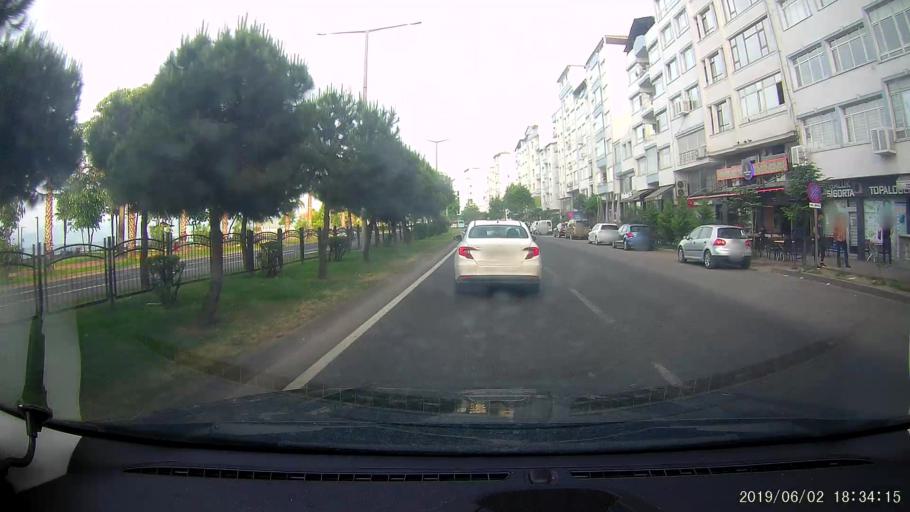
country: TR
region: Ordu
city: Fatsa
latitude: 41.0303
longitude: 37.5023
